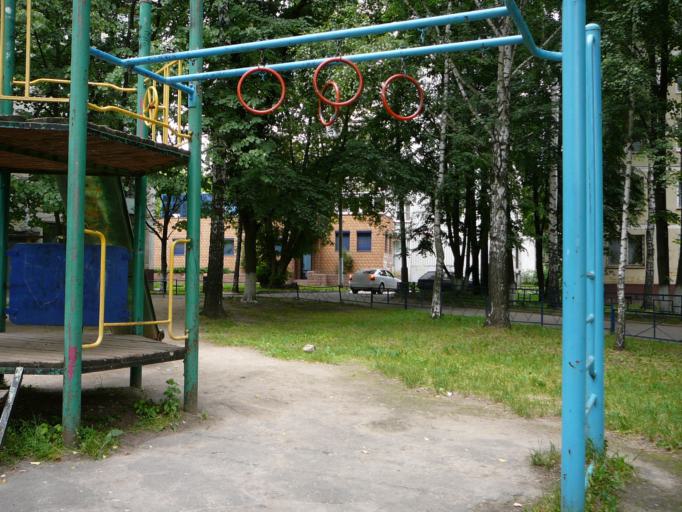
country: RU
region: Moskovskaya
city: Krasnogorsk
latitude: 55.8158
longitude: 37.3091
